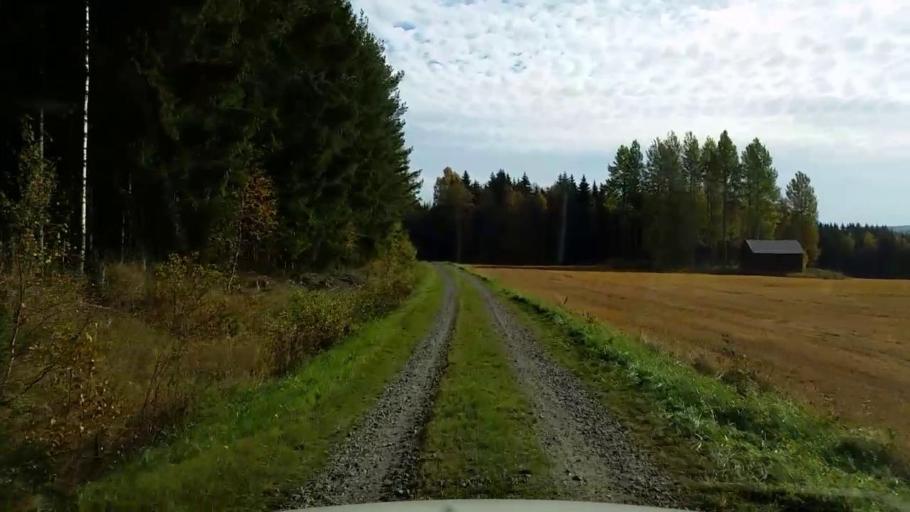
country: SE
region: Gaevleborg
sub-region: Ljusdals Kommun
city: Jaervsoe
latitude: 61.7821
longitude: 16.1722
